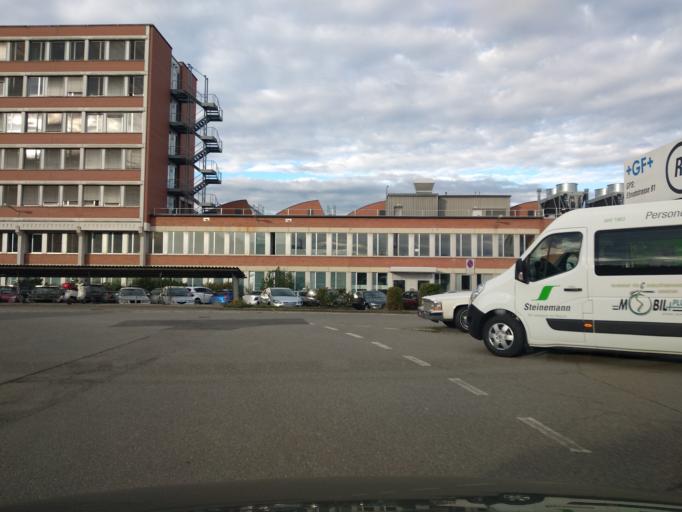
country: CH
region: Schaffhausen
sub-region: Bezirk Schaffhausen
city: Schaffhausen
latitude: 47.7108
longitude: 8.6500
